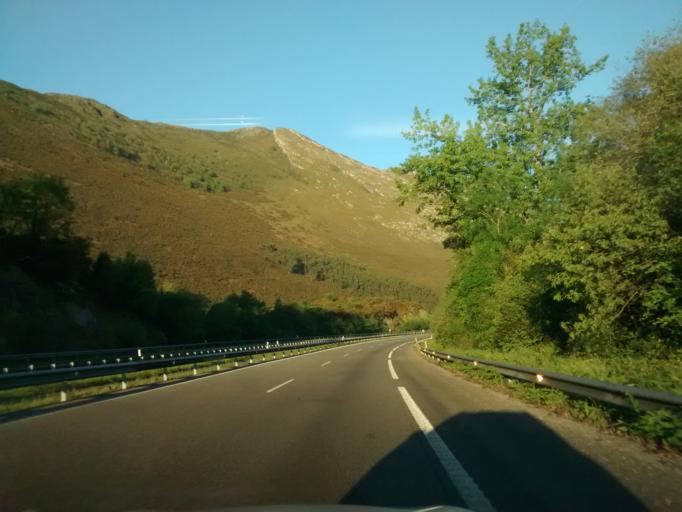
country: ES
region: Asturias
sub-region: Province of Asturias
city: Ribadesella
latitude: 43.4355
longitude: -4.9938
